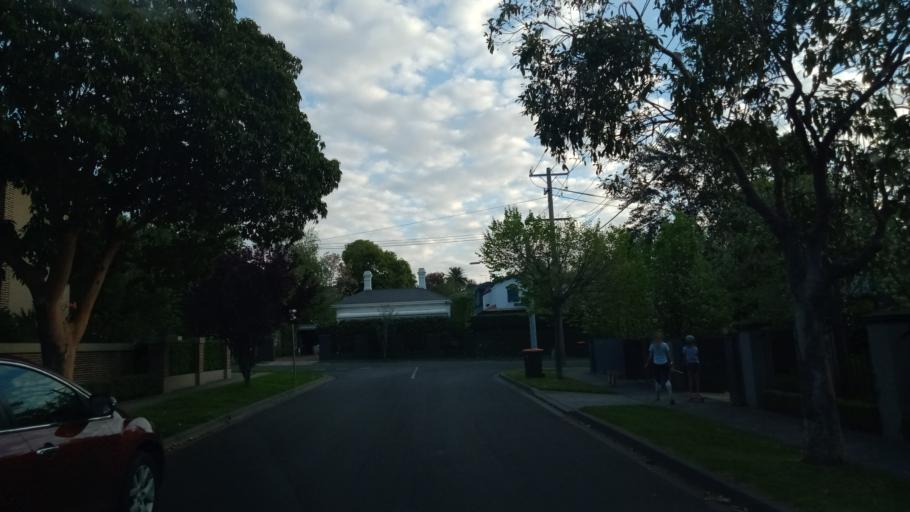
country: AU
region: Victoria
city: Glenferrie
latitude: -37.8362
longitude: 145.0516
